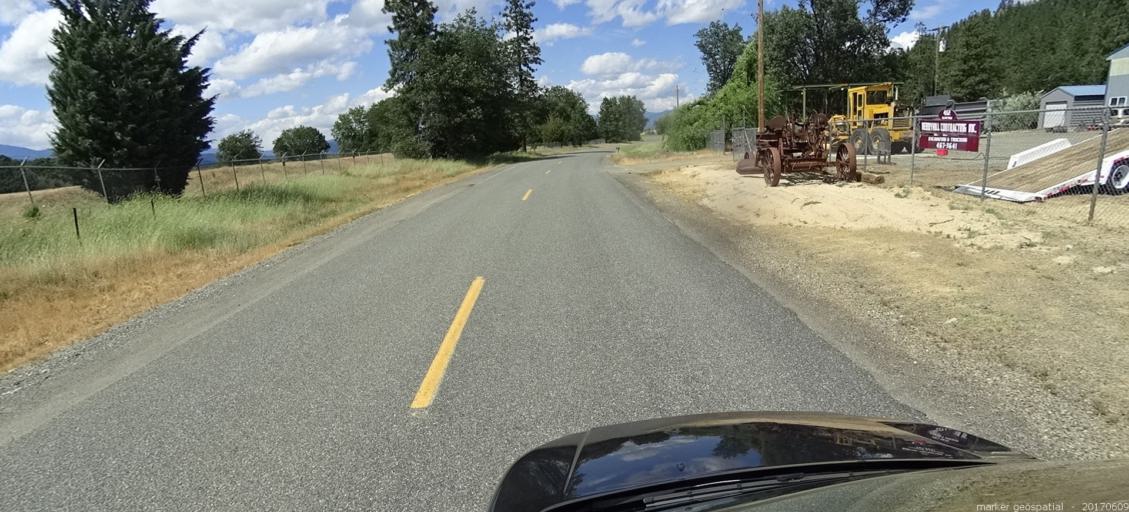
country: US
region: California
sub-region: Siskiyou County
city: Yreka
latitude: 41.4654
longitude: -122.8837
